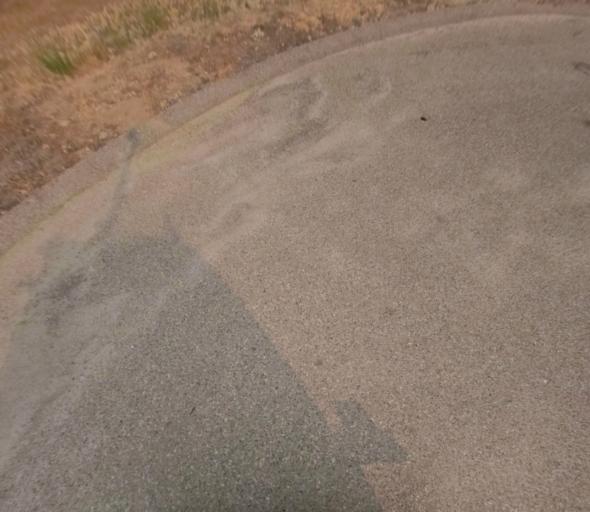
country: US
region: California
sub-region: Madera County
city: Coarsegold
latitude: 37.2159
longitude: -119.7199
